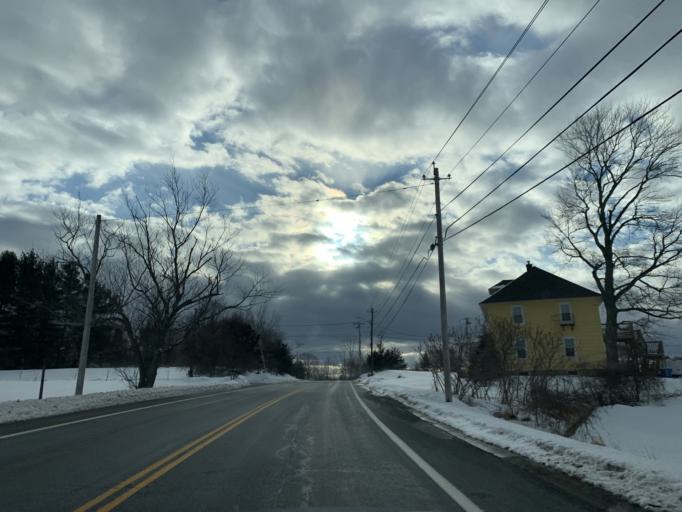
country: US
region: Rhode Island
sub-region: Providence County
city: Cumberland Hill
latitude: 42.0072
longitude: -71.4501
